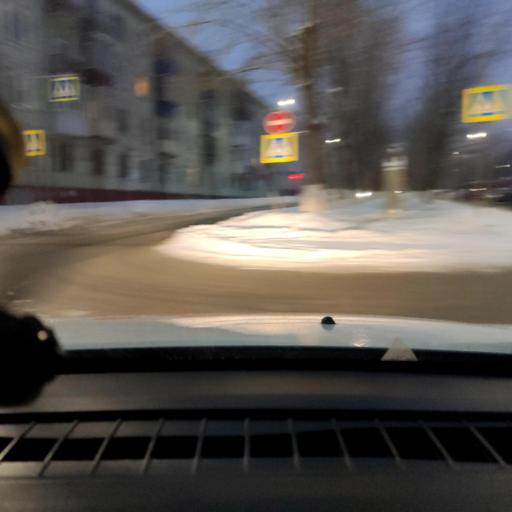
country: RU
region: Samara
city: Novokuybyshevsk
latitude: 53.0971
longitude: 49.9542
